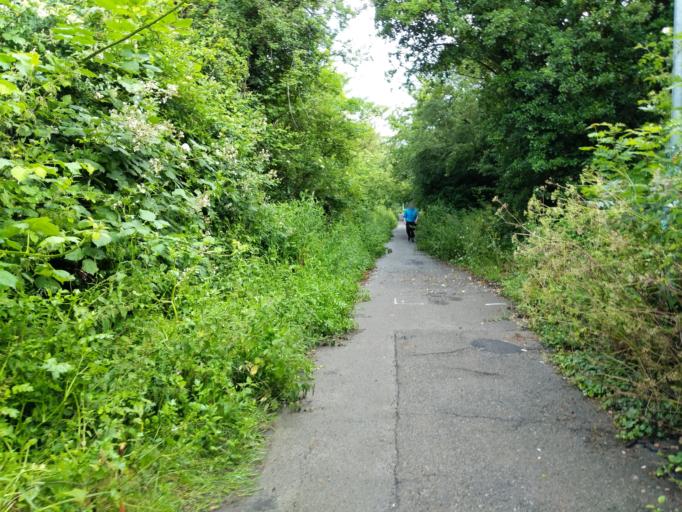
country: GB
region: England
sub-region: Kent
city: Tankerton
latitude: 51.3537
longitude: 1.0400
